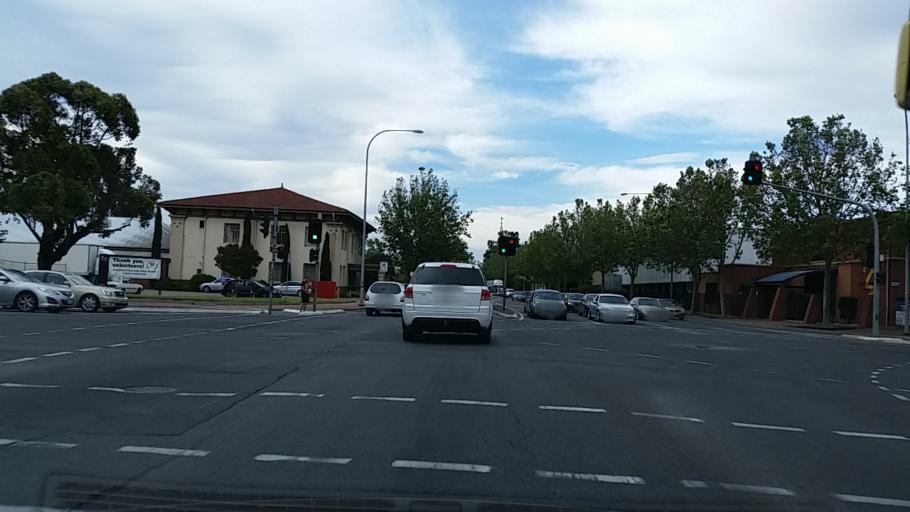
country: AU
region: South Australia
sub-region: City of West Torrens
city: Thebarton
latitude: -34.9239
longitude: 138.5697
